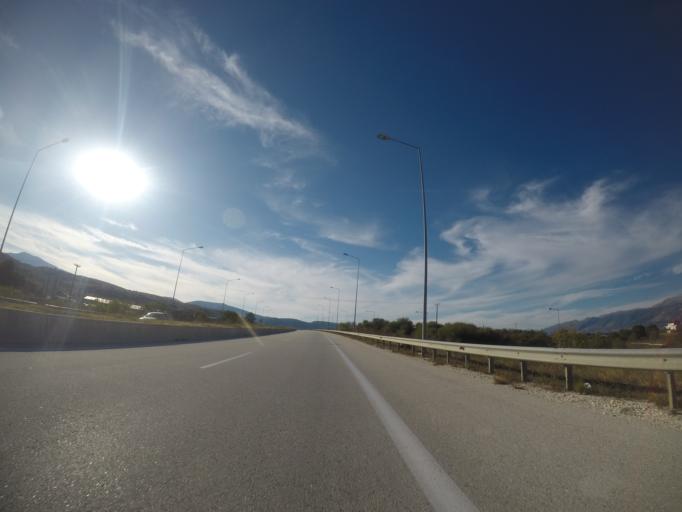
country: GR
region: Epirus
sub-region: Nomos Ioanninon
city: Koutselio
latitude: 39.5996
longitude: 20.9084
